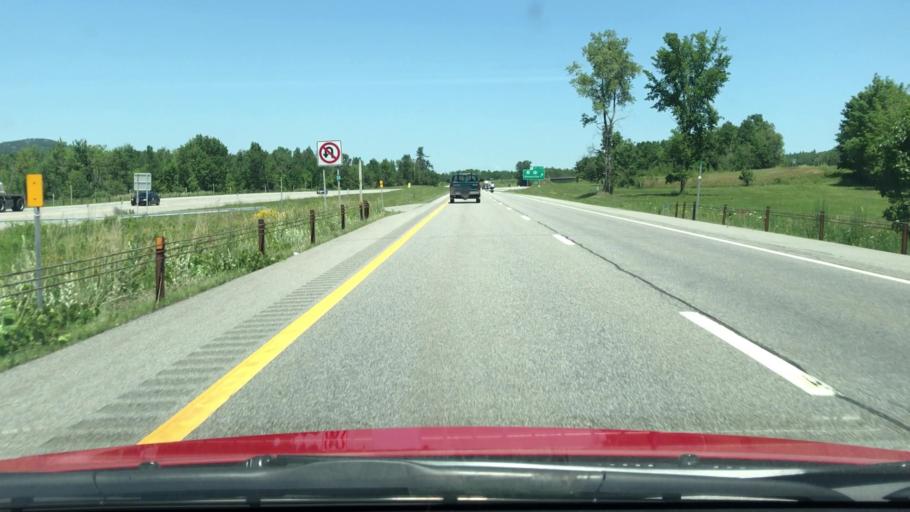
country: US
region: New York
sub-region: Essex County
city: Keeseville
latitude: 44.4371
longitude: -73.4918
